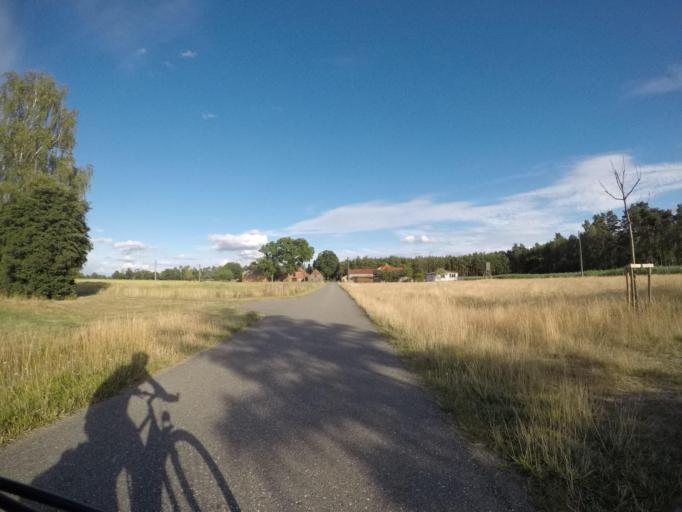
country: DE
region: Mecklenburg-Vorpommern
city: Lubtheen
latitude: 53.2370
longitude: 11.0380
